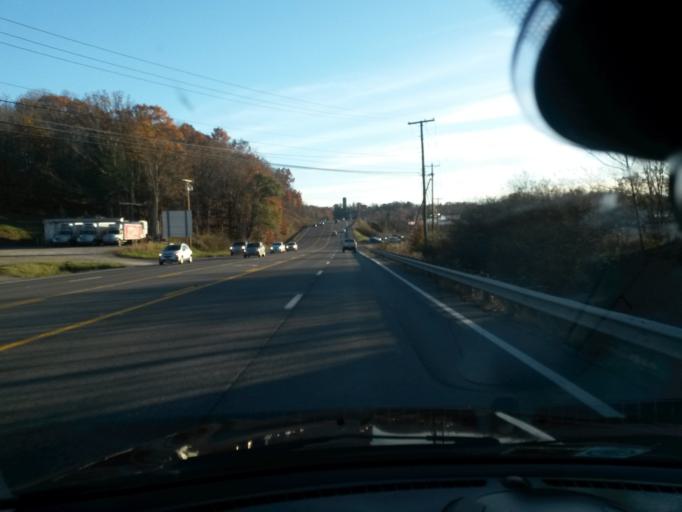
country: US
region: West Virginia
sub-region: Raleigh County
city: Prosperity
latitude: 37.8395
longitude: -81.1937
